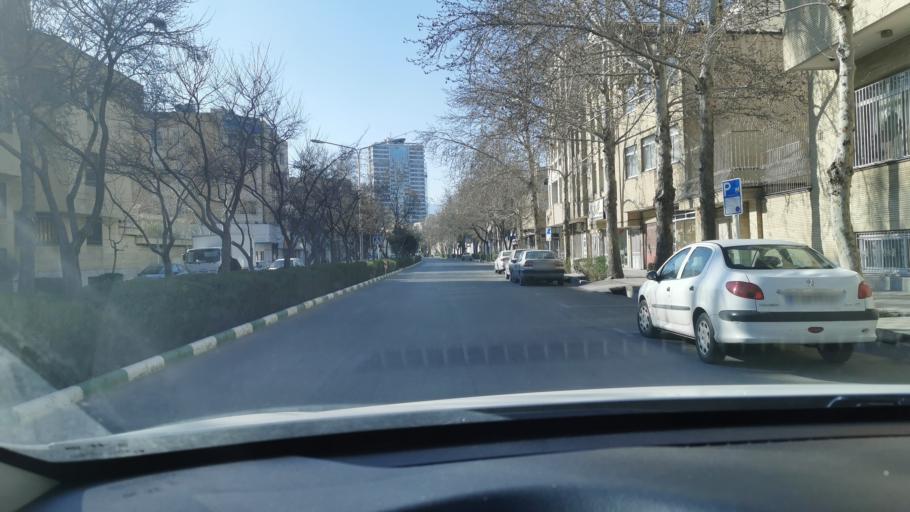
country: IR
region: Razavi Khorasan
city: Mashhad
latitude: 36.2891
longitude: 59.5673
